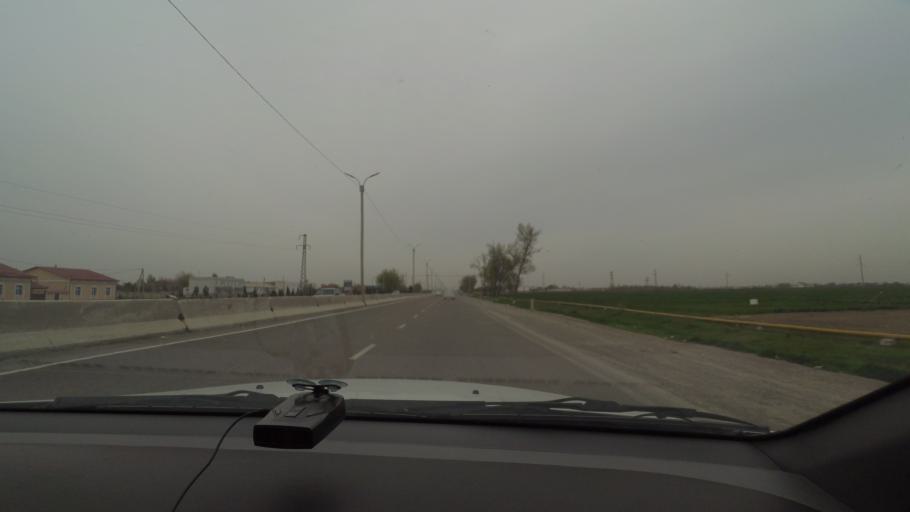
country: KZ
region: Ongtustik Qazaqstan
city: Myrzakent
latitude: 40.5522
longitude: 68.3987
